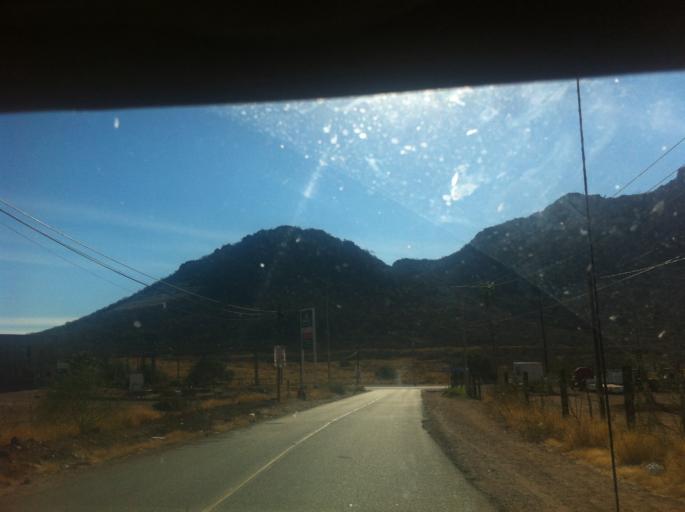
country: MX
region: Sonora
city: Heroica Guaymas
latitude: 27.9271
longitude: -110.9330
